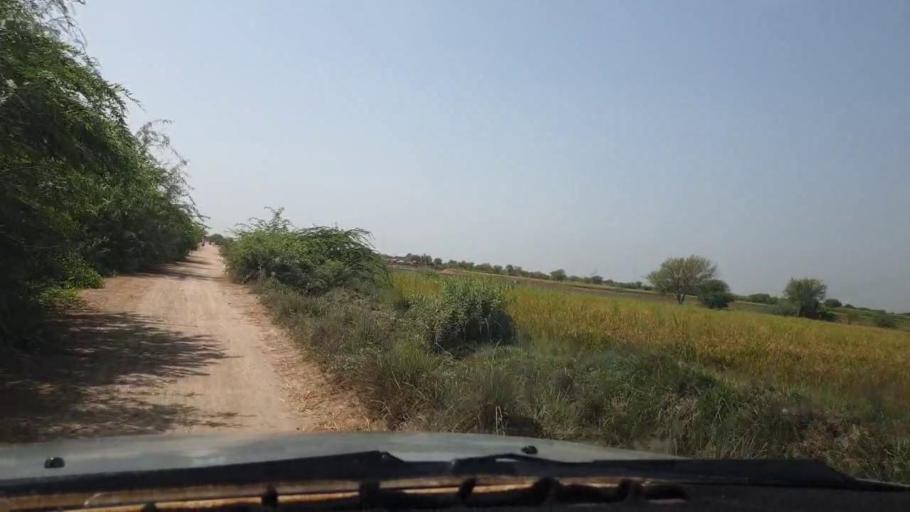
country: PK
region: Sindh
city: Tando Ghulam Ali
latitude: 25.1438
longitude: 68.7749
